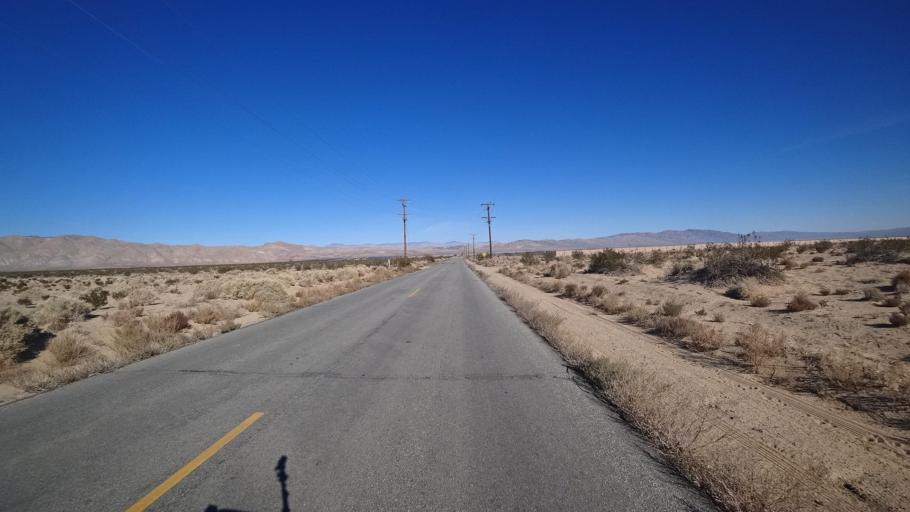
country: US
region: California
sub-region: Kern County
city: California City
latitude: 35.2416
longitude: -117.9860
